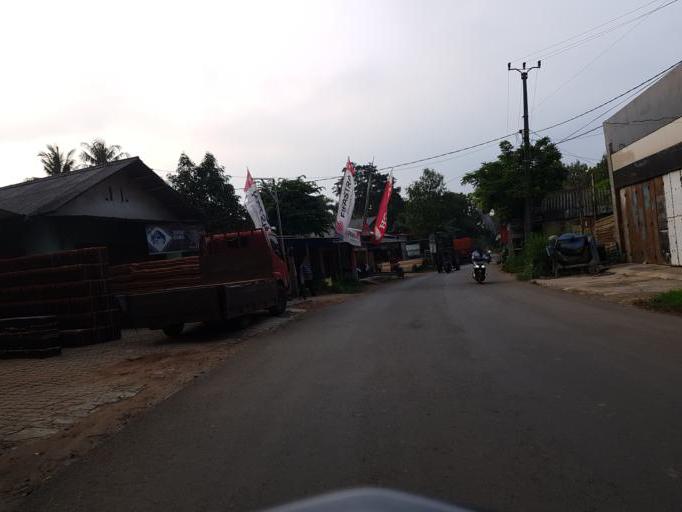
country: ID
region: West Java
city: Parung
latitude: -6.4680
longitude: 106.7121
